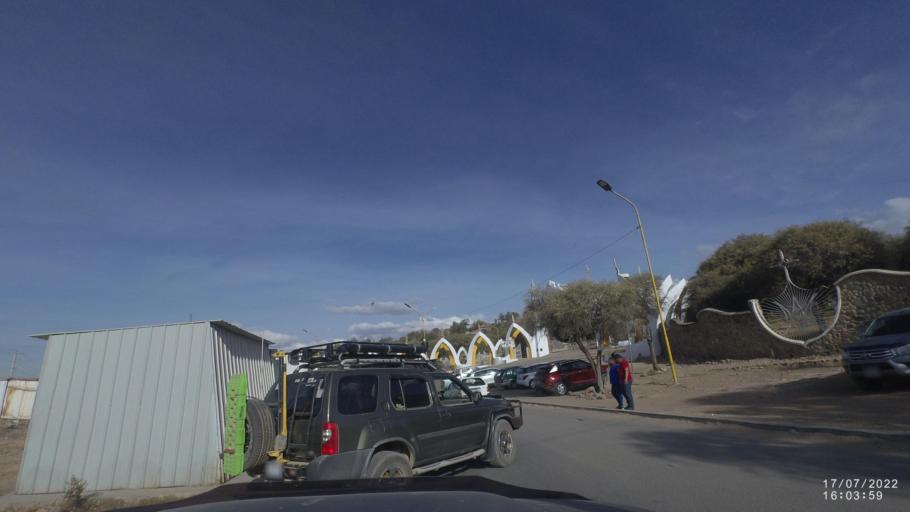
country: BO
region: Cochabamba
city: Sipe Sipe
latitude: -17.4199
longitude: -66.2842
